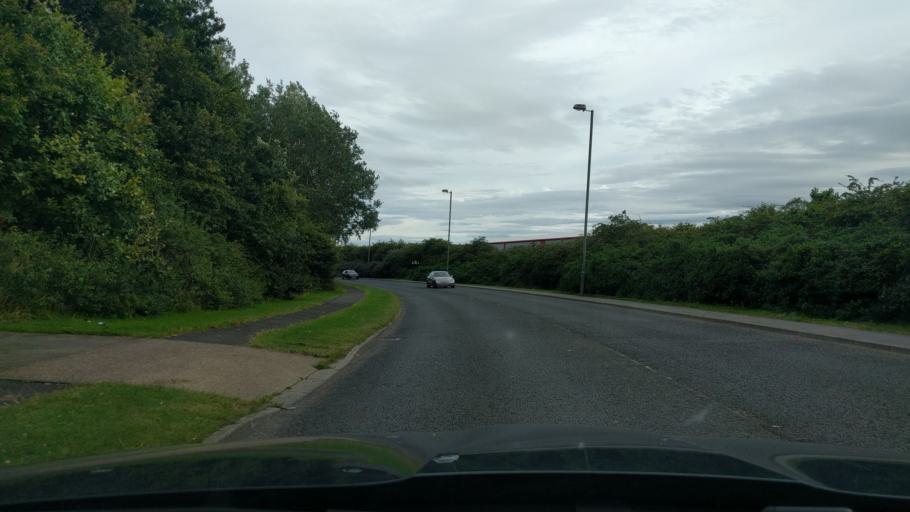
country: GB
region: England
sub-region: Borough of North Tyneside
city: Shiremoor
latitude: 55.0234
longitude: -1.4935
